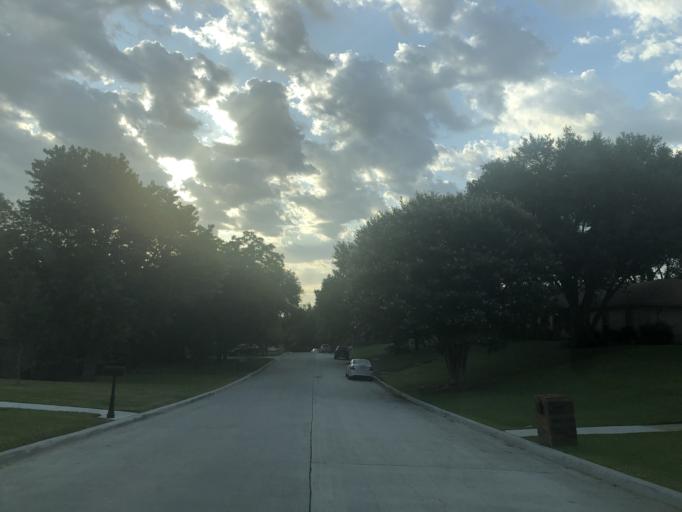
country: US
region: Texas
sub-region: Dallas County
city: Grand Prairie
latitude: 32.7631
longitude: -97.0231
